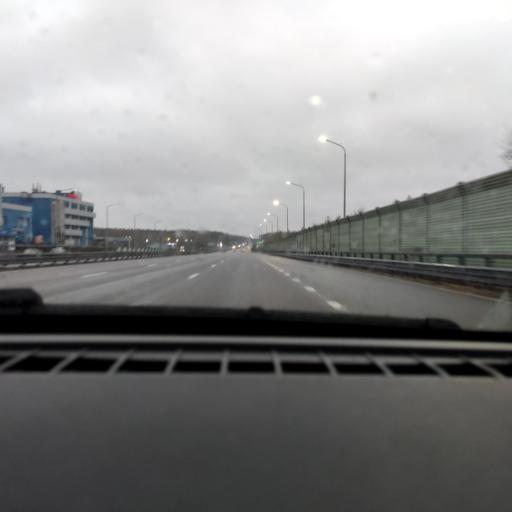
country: RU
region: Voronezj
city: Somovo
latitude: 51.6806
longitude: 39.3018
